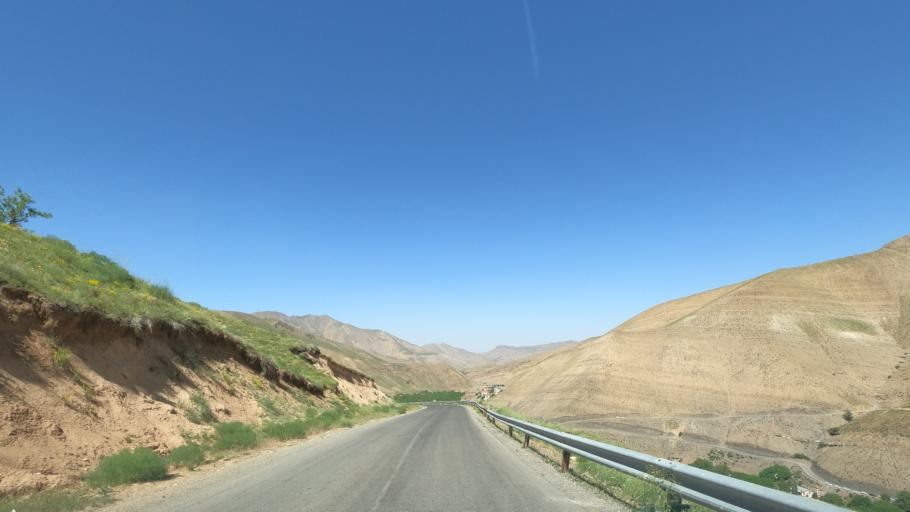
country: IR
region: Alborz
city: Karaj
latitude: 35.9236
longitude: 51.1607
